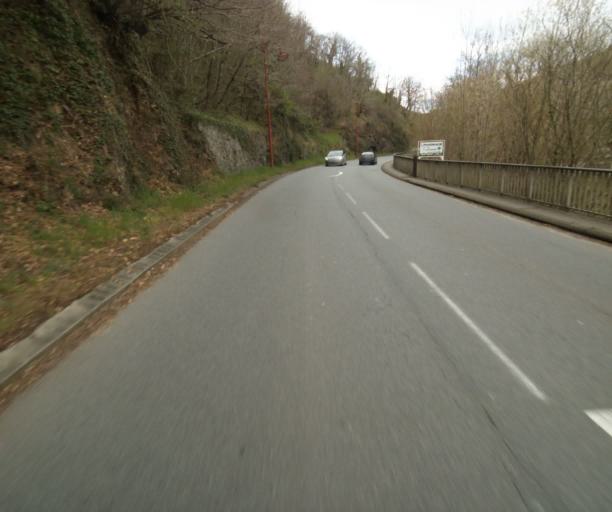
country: FR
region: Limousin
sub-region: Departement de la Correze
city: Laguenne
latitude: 45.2462
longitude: 1.7745
